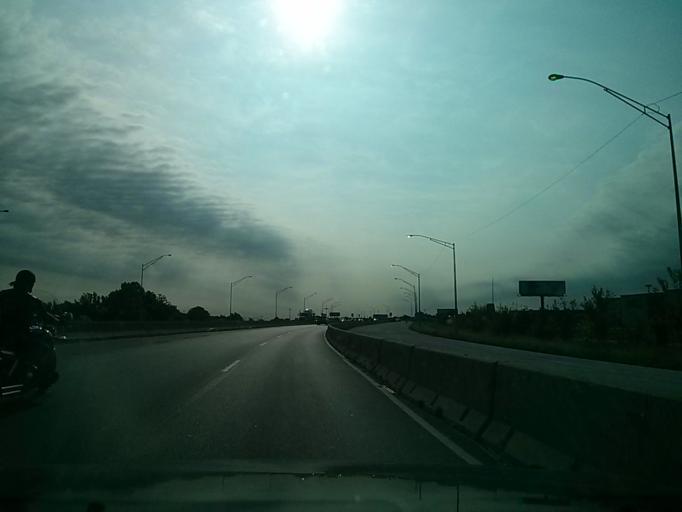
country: US
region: Oklahoma
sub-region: Tulsa County
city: Tulsa
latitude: 36.1629
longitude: -95.9005
